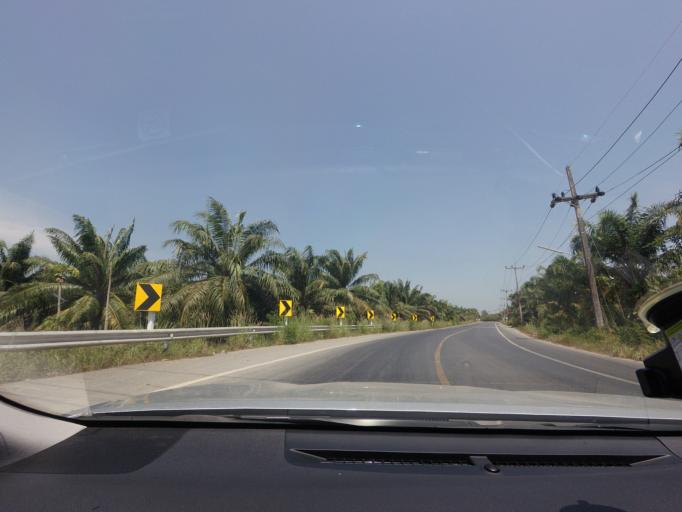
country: TH
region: Surat Thani
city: Tha Chang
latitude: 9.1967
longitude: 99.2466
